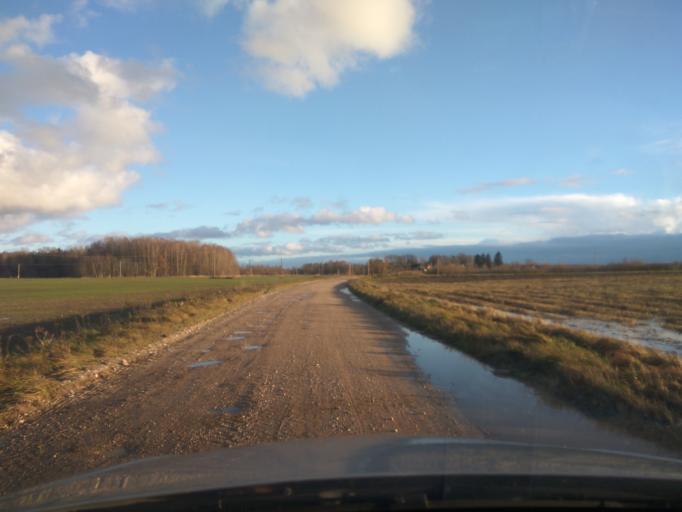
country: LV
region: Aizpute
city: Aizpute
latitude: 56.7721
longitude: 21.7009
